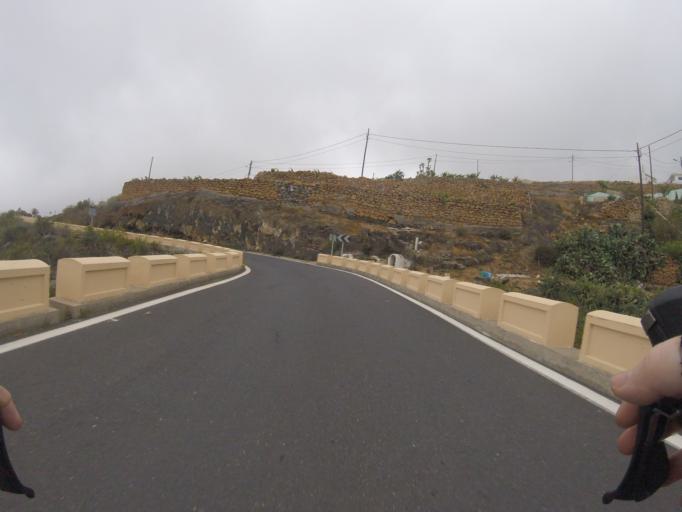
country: ES
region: Canary Islands
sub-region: Provincia de Santa Cruz de Tenerife
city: Lomo de Arico
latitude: 28.1944
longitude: -16.4774
